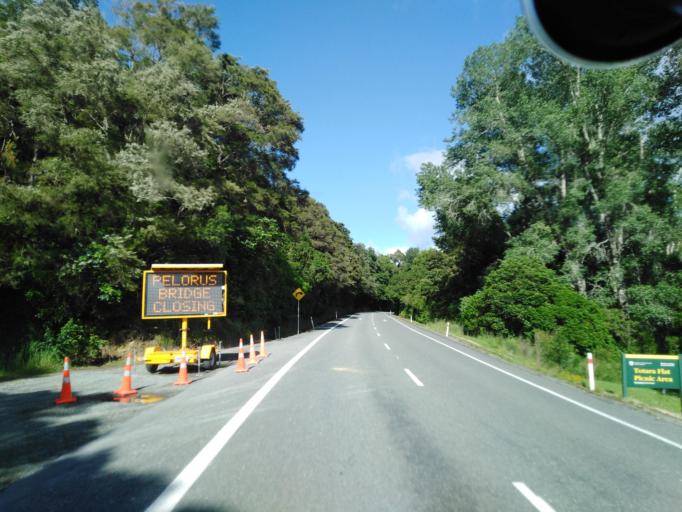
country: NZ
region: Nelson
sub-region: Nelson City
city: Nelson
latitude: -41.3014
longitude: 173.5776
